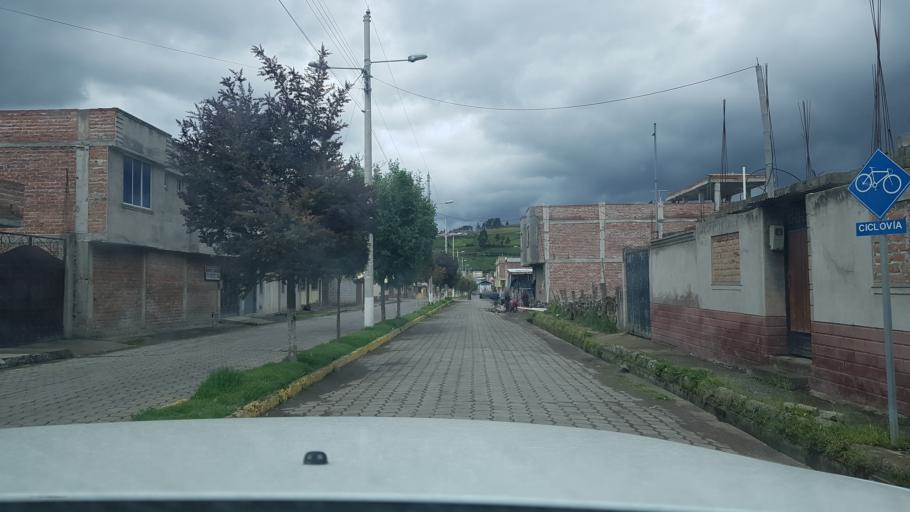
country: EC
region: Chimborazo
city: Riobamba
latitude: -1.7047
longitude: -78.7751
